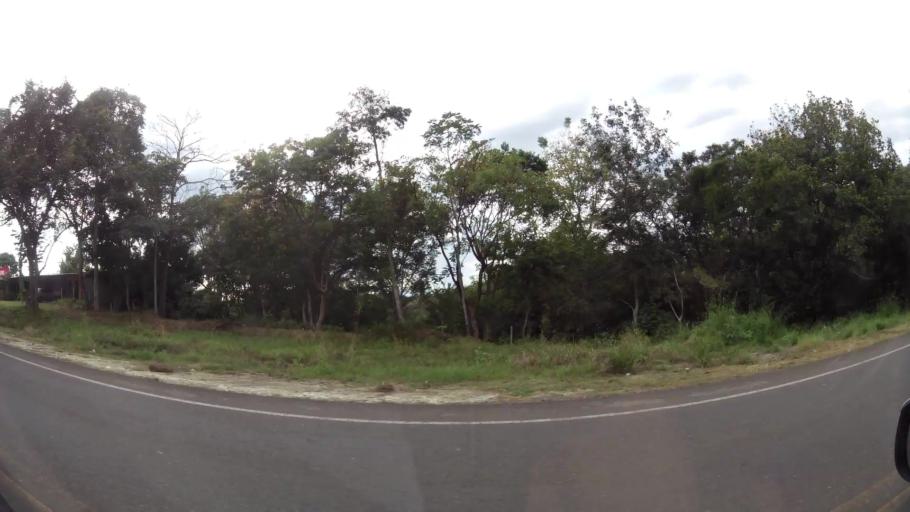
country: CR
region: Alajuela
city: Orotina
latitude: 9.8710
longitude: -84.5731
